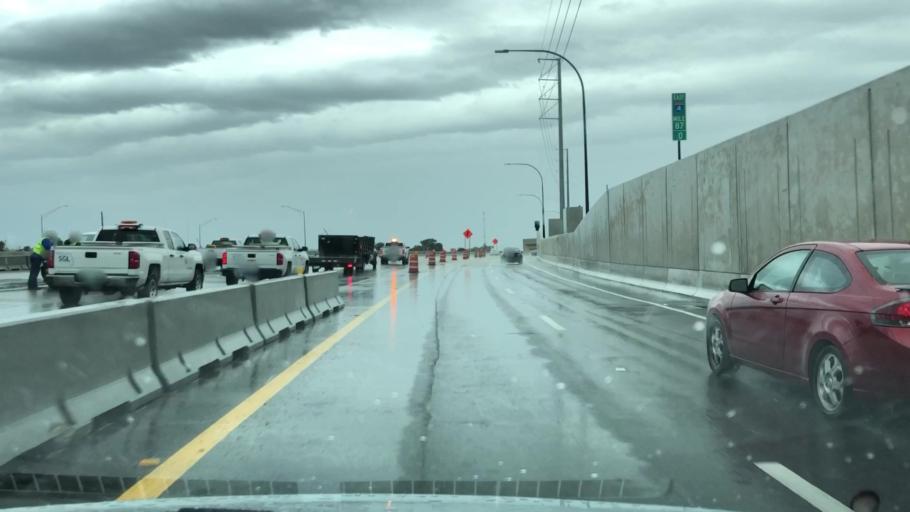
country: US
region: Florida
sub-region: Orange County
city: Fairview Shores
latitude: 28.5957
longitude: -81.3844
